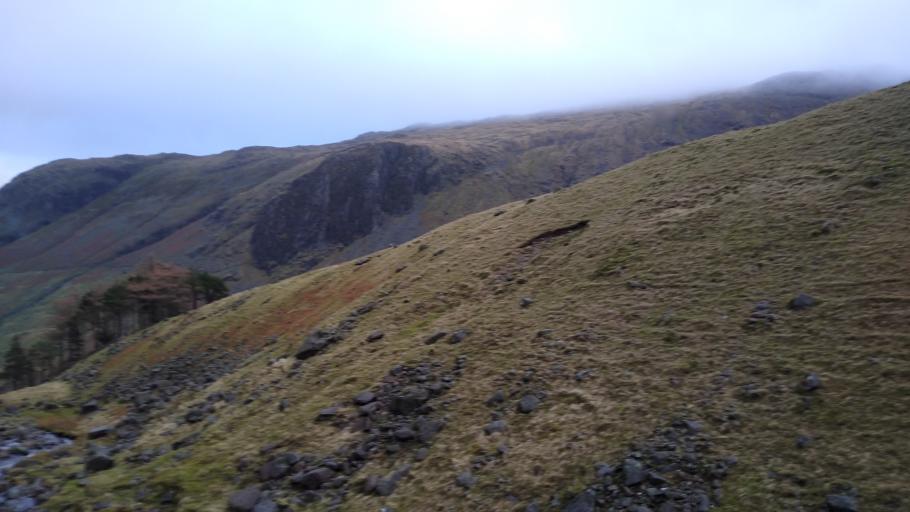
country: GB
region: England
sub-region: Cumbria
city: Keswick
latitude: 54.4867
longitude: -3.1932
